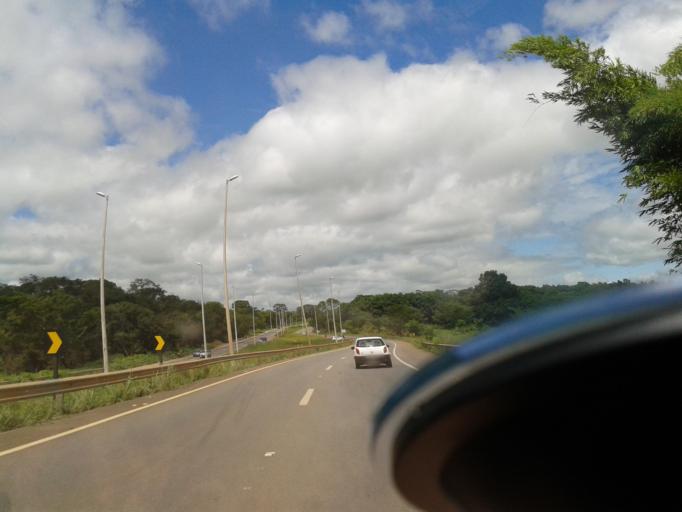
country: BR
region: Goias
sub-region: Inhumas
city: Inhumas
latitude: -16.4037
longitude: -49.4835
